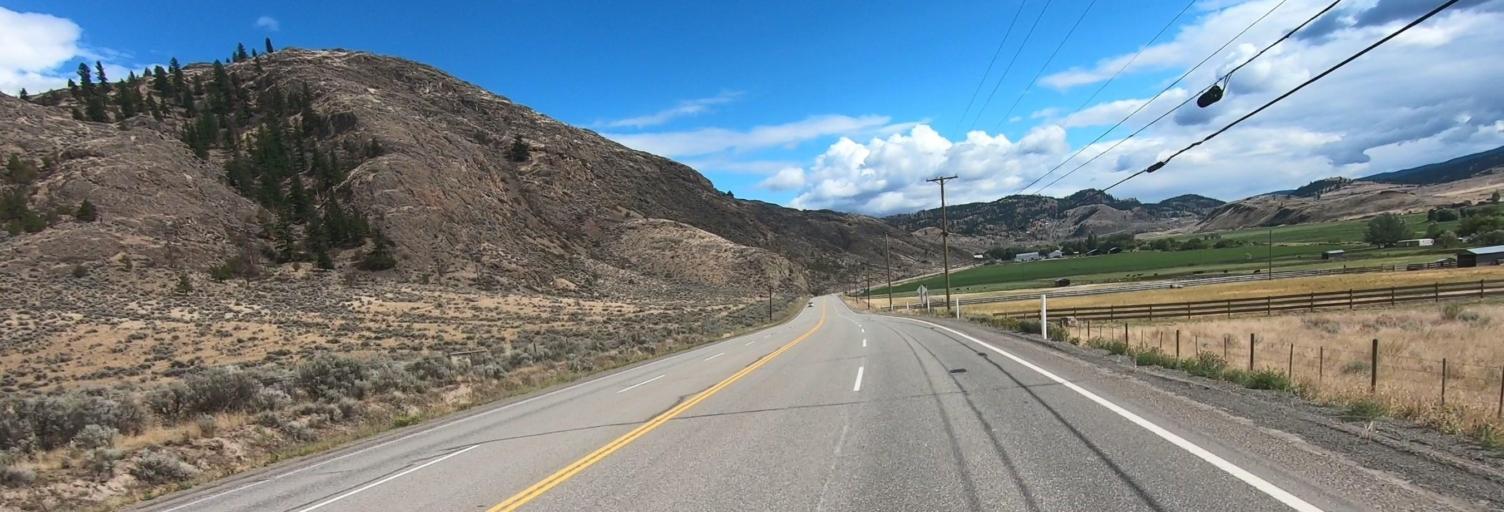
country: CA
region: British Columbia
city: Logan Lake
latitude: 50.7114
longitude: -120.6200
